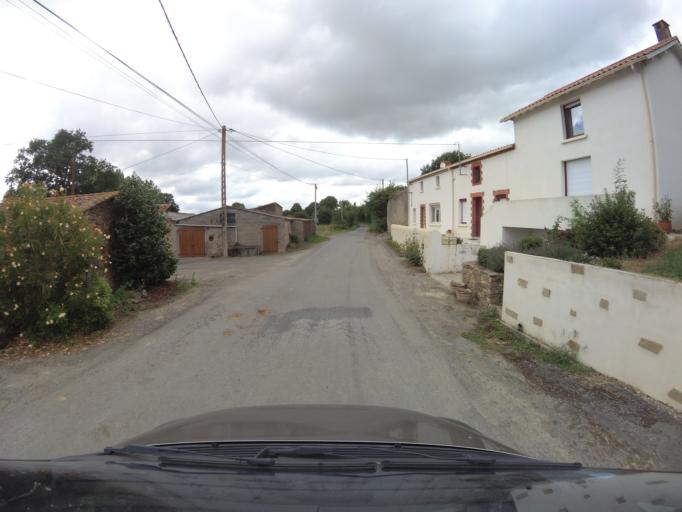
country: FR
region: Pays de la Loire
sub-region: Departement de la Loire-Atlantique
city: Vieillevigne
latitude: 46.9902
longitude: -1.4750
